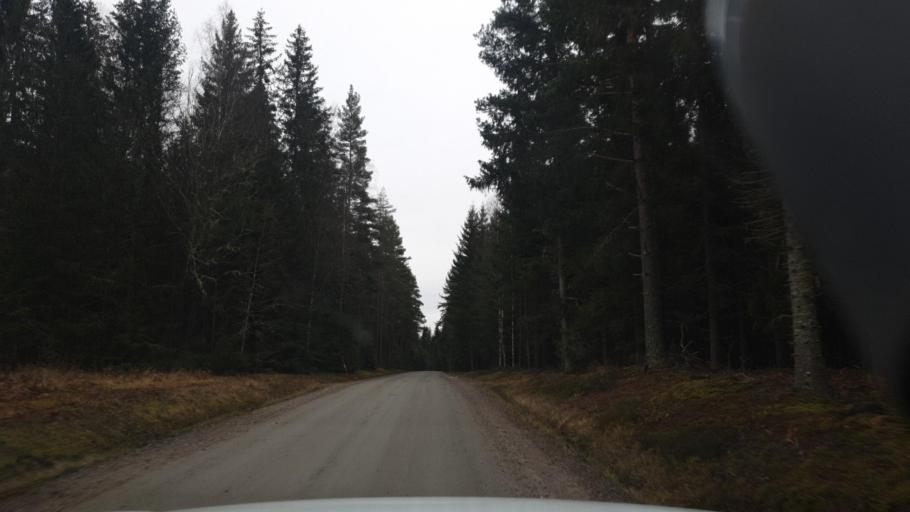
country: SE
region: Vaermland
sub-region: Karlstads Kommun
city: Edsvalla
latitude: 59.4972
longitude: 13.0289
